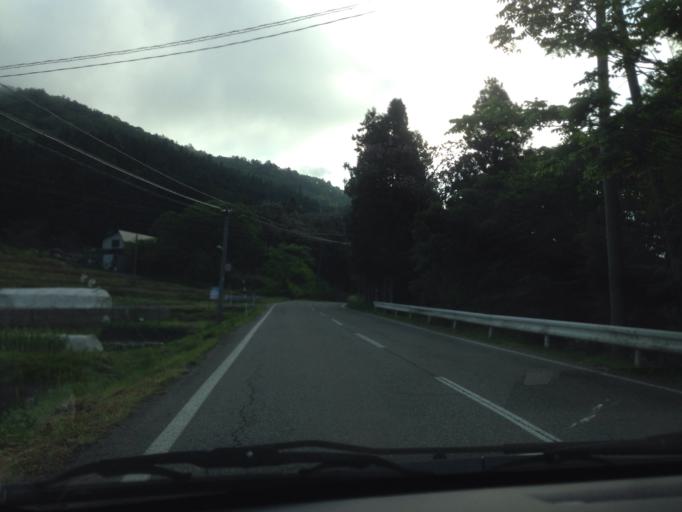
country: JP
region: Fukushima
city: Inawashiro
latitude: 37.3078
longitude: 139.9112
